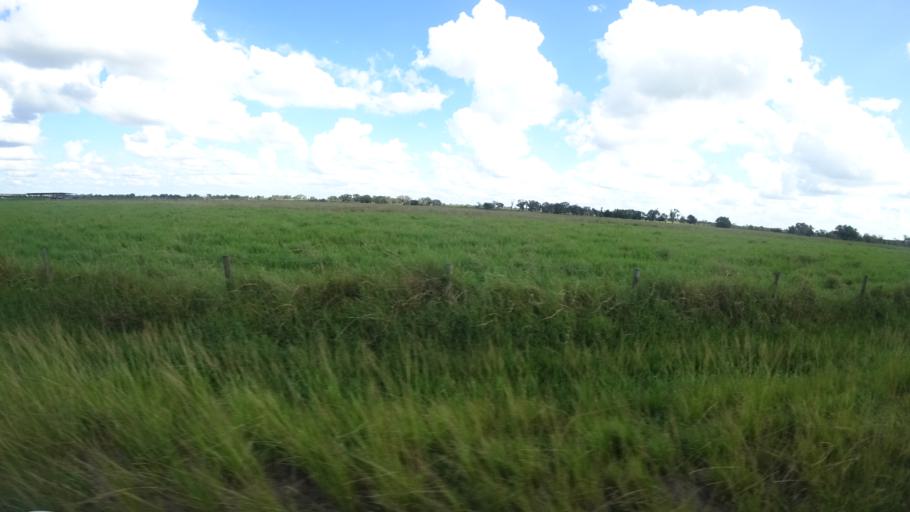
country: US
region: Florida
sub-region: DeSoto County
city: Nocatee
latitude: 27.2869
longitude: -82.1135
